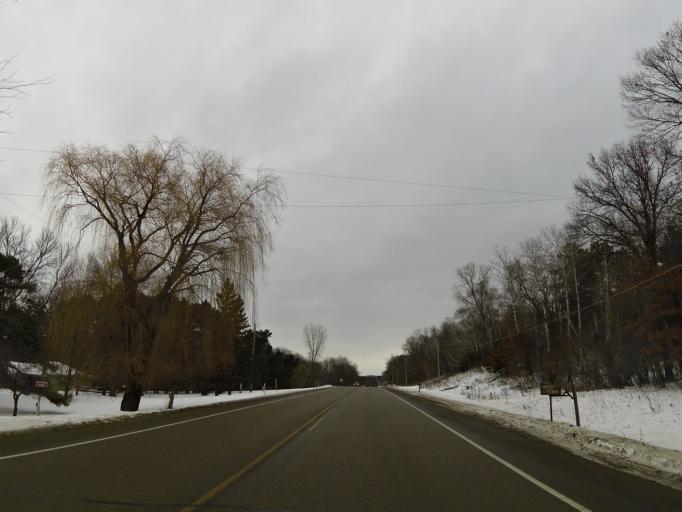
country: US
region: Wisconsin
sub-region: Saint Croix County
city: North Hudson
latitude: 45.0100
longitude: -92.7501
